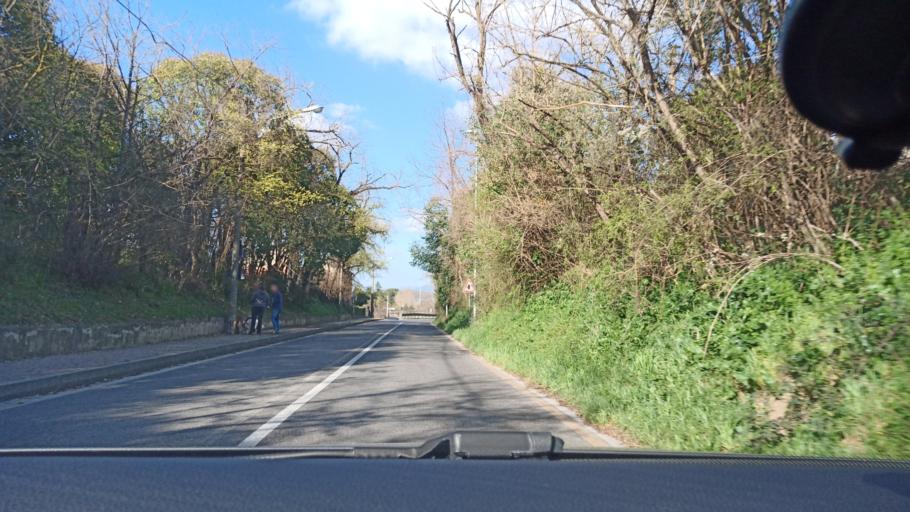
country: IT
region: Latium
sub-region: Citta metropolitana di Roma Capitale
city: Torrita Tiberina
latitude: 42.2465
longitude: 12.6349
